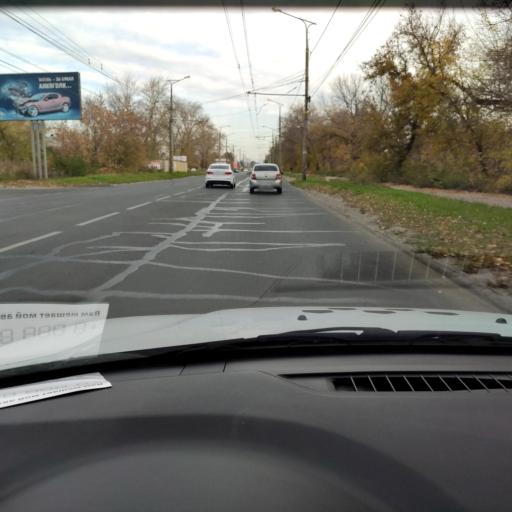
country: RU
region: Samara
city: Tol'yatti
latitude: 53.5283
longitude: 49.4366
